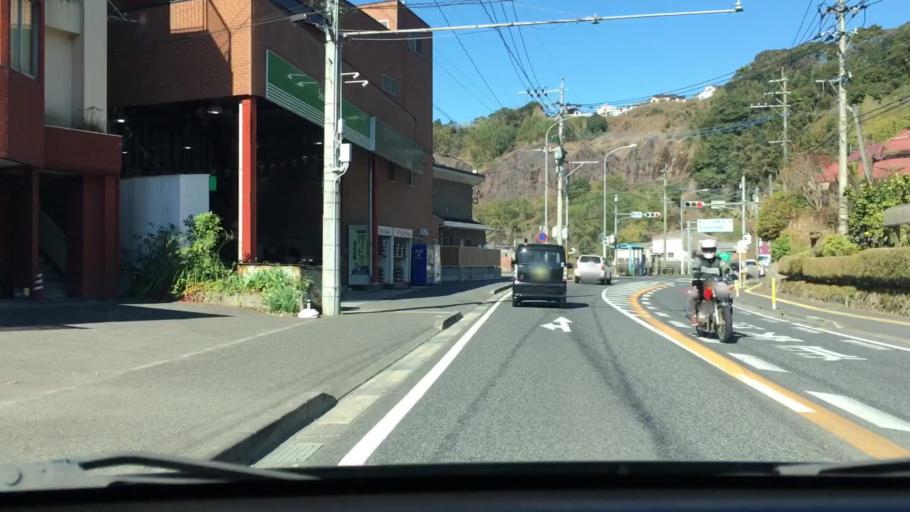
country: JP
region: Kagoshima
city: Kagoshima-shi
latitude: 31.6313
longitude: 130.5241
